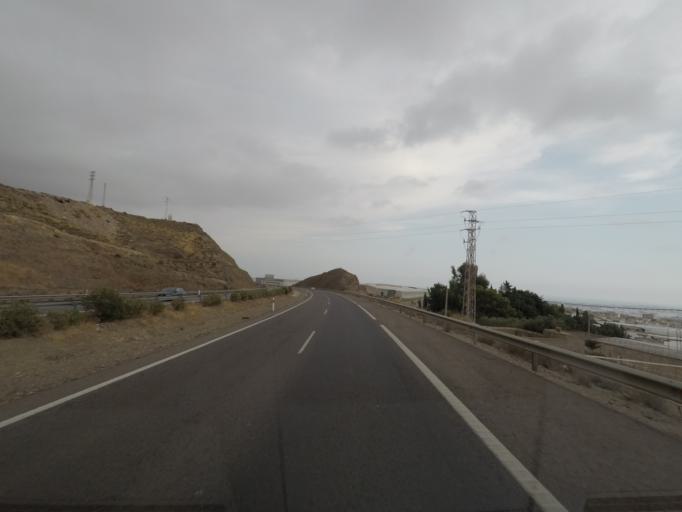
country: ES
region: Andalusia
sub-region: Provincia de Almeria
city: Vicar
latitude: 36.8117
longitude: -2.6387
